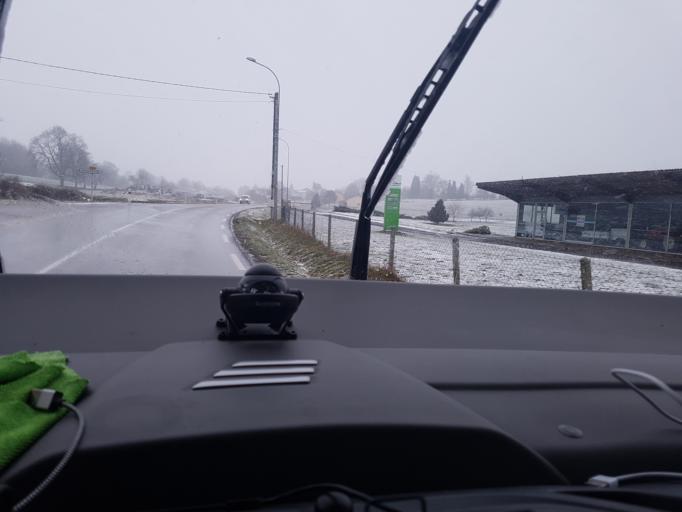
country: FR
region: Lorraine
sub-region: Departement de Meurthe-et-Moselle
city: Baccarat
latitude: 48.4854
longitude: 6.7827
